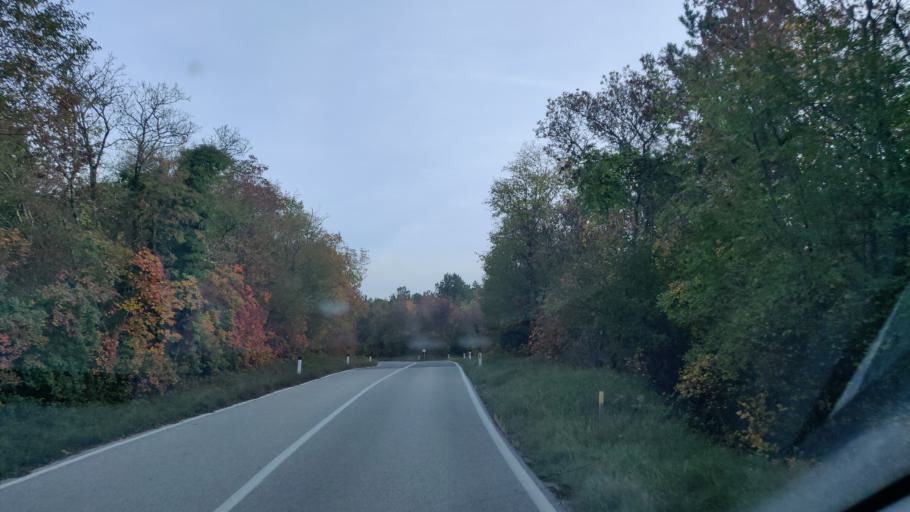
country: SI
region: Rence-Vogrsko
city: Rence
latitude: 45.8347
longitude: 13.6530
